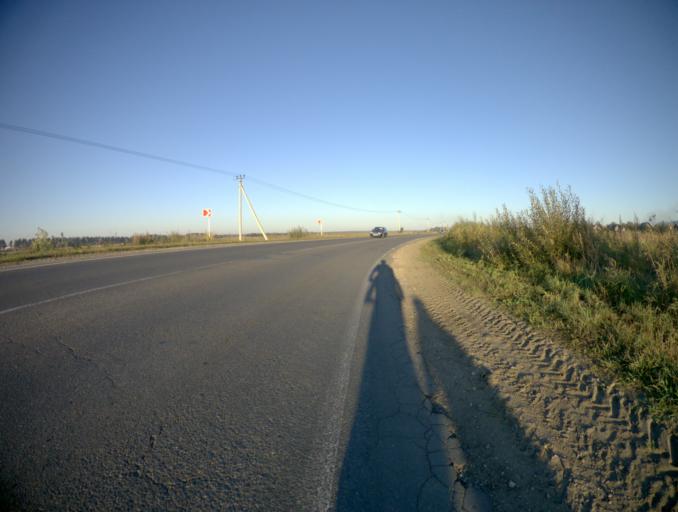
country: RU
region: Vladimir
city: Raduzhnyy
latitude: 56.0232
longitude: 40.3234
